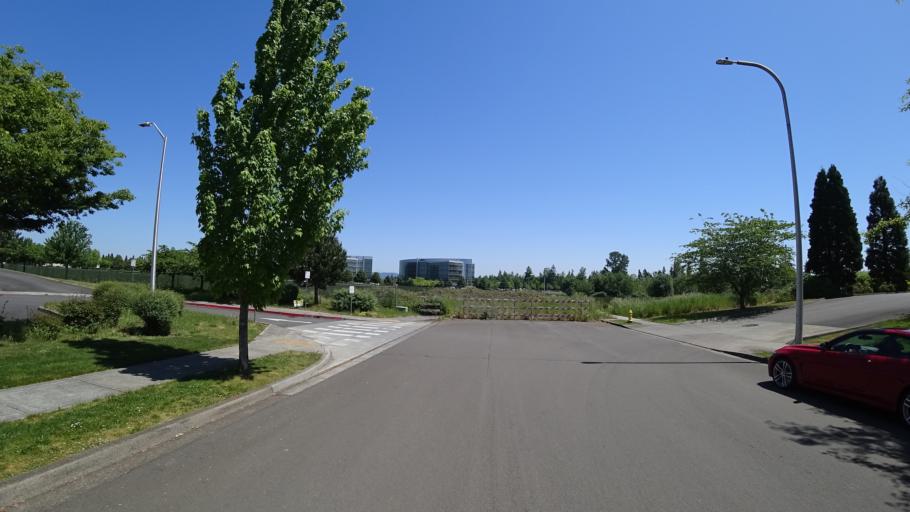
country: US
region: Oregon
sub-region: Washington County
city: Rockcreek
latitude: 45.5322
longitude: -122.9075
